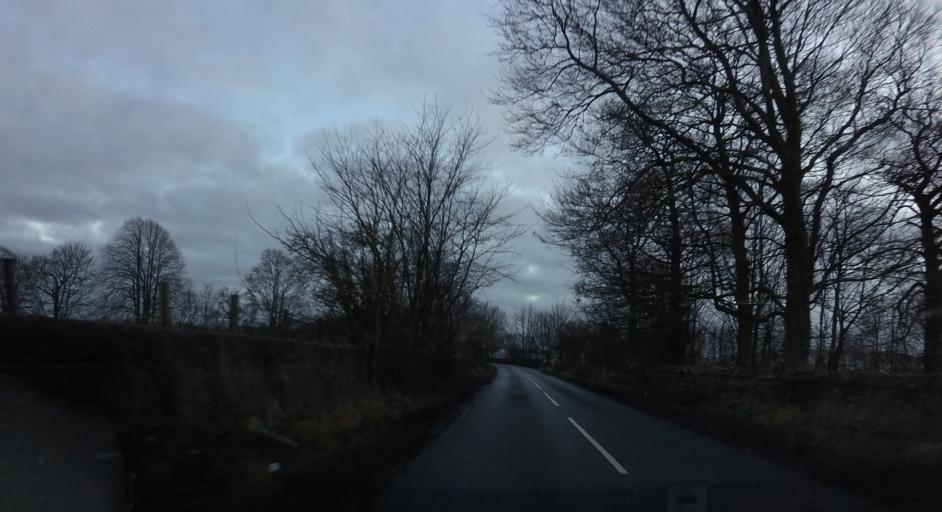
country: GB
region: Scotland
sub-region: Fife
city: Crossford
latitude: 56.0545
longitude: -3.4911
